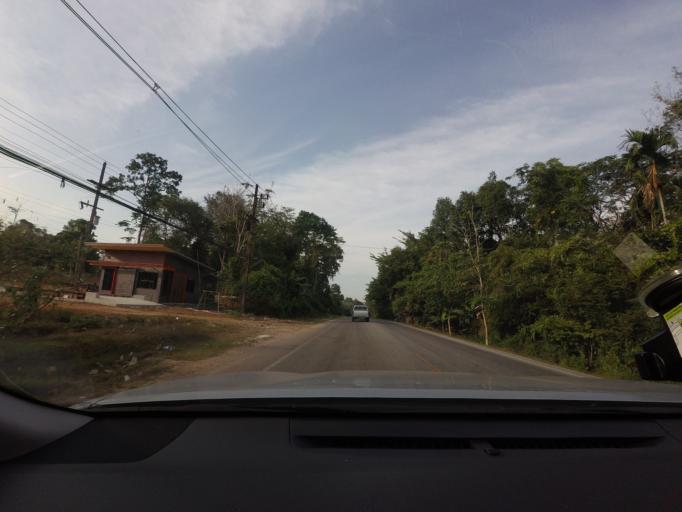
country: TH
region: Narathiwat
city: Ra-ngae
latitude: 6.3070
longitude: 101.7277
